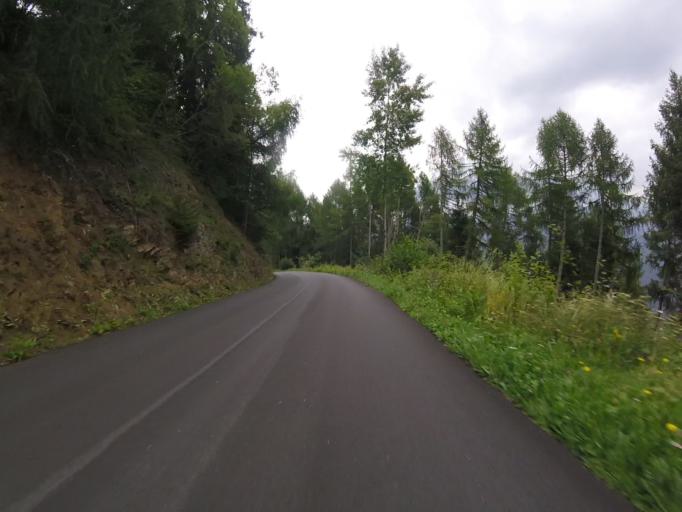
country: IT
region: Lombardy
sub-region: Provincia di Brescia
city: Monno
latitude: 46.2195
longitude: 10.3315
